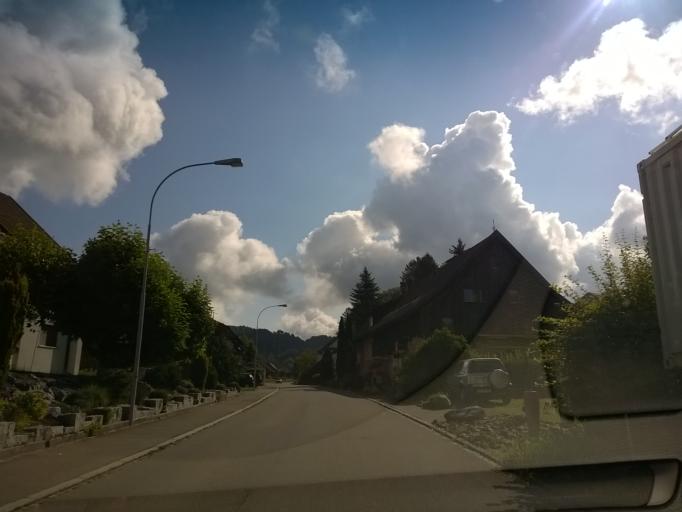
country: CH
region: Zurich
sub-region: Bezirk Buelach
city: Embrach / Embrach (Dorfkern)
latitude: 47.4878
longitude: 8.6199
